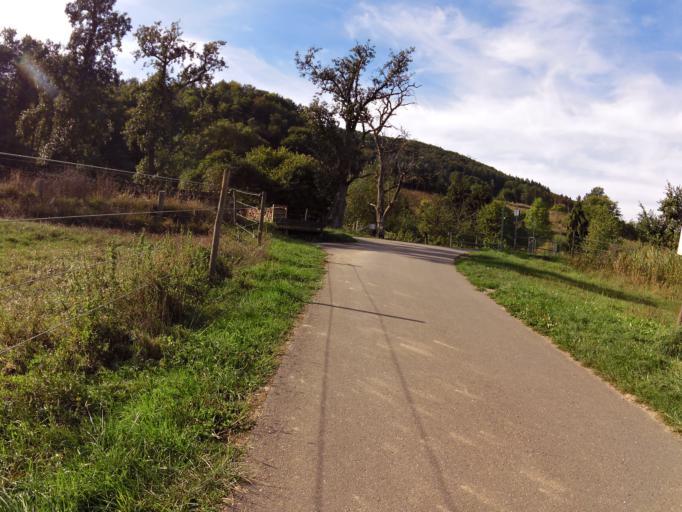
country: DE
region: Rheinland-Pfalz
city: Prumzurlay
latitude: 49.8640
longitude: 6.4368
